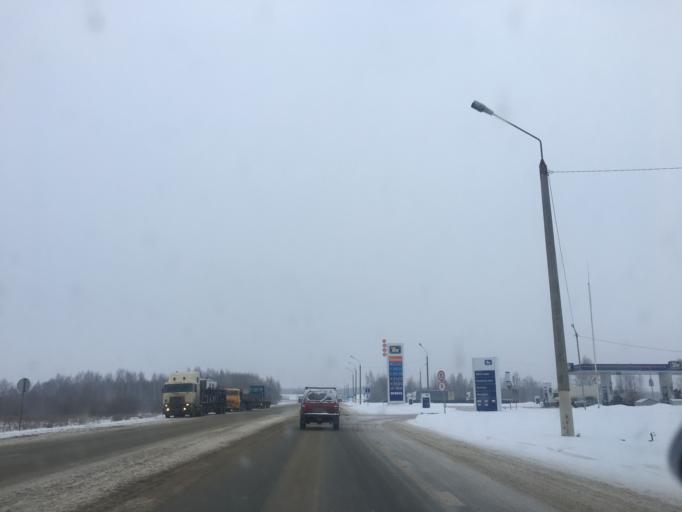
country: RU
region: Tula
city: Kosaya Gora
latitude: 54.1631
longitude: 37.4958
